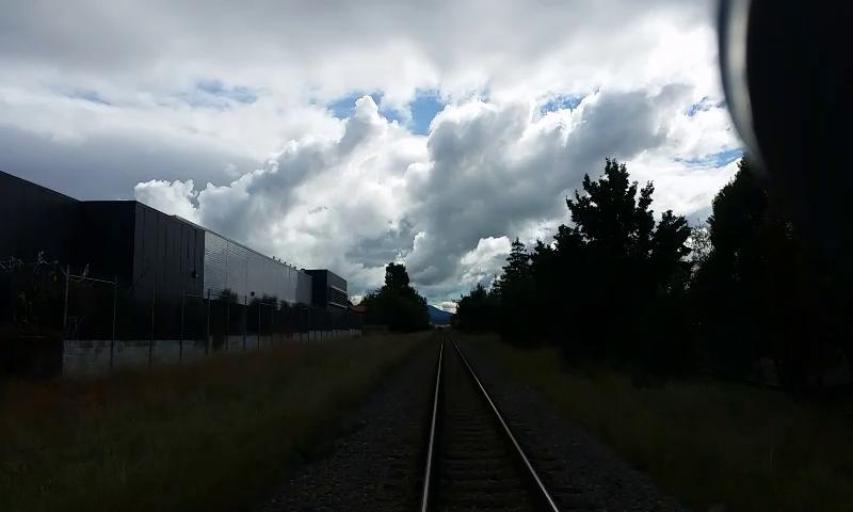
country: NZ
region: Canterbury
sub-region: Waimakariri District
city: Woodend
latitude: -43.3079
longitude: 172.5995
